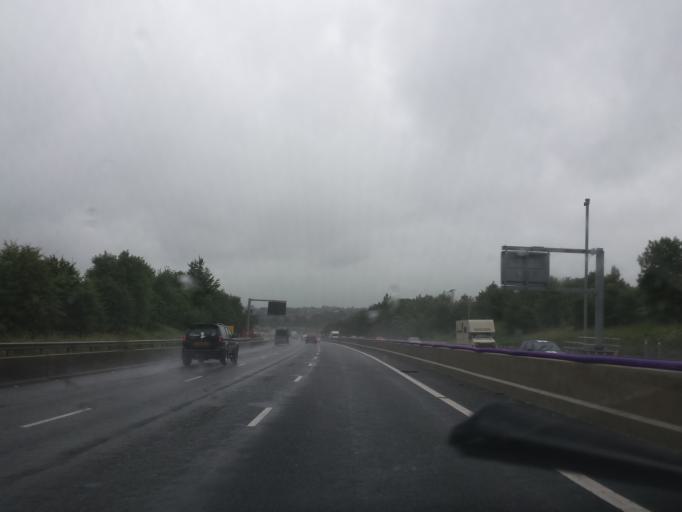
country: GB
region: England
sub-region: Derbyshire
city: Blackwell
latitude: 53.1202
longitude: -1.3335
